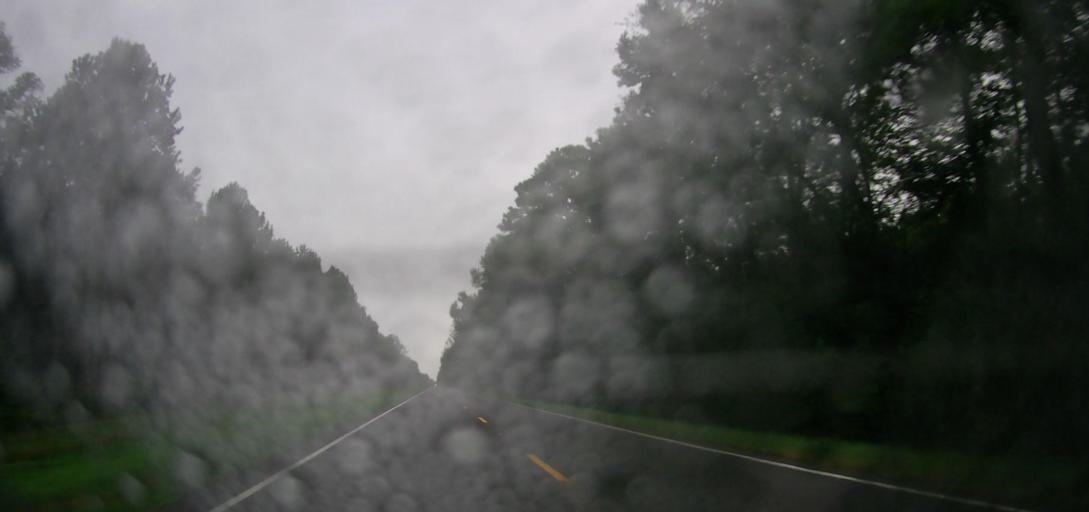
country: US
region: Georgia
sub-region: Glynn County
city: Dock Junction
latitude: 31.2598
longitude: -81.6212
